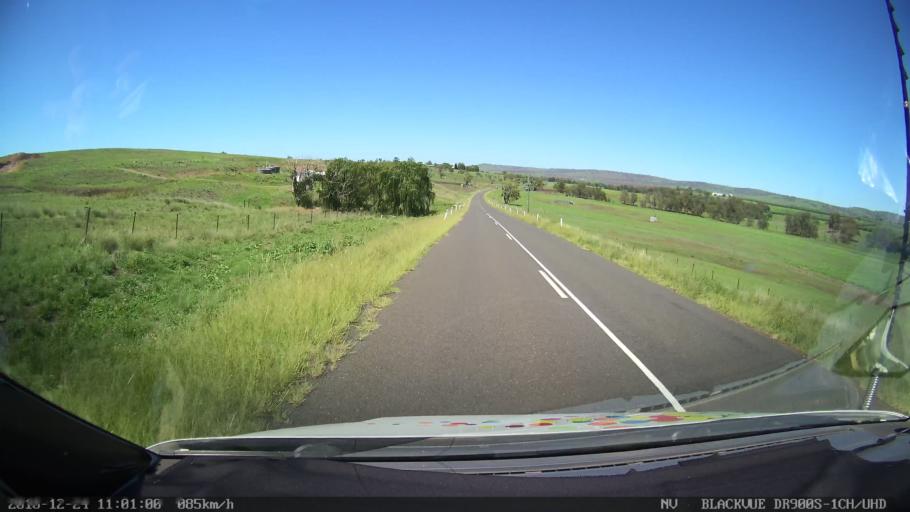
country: AU
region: New South Wales
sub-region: Upper Hunter Shire
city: Merriwa
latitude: -32.0721
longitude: 150.3890
